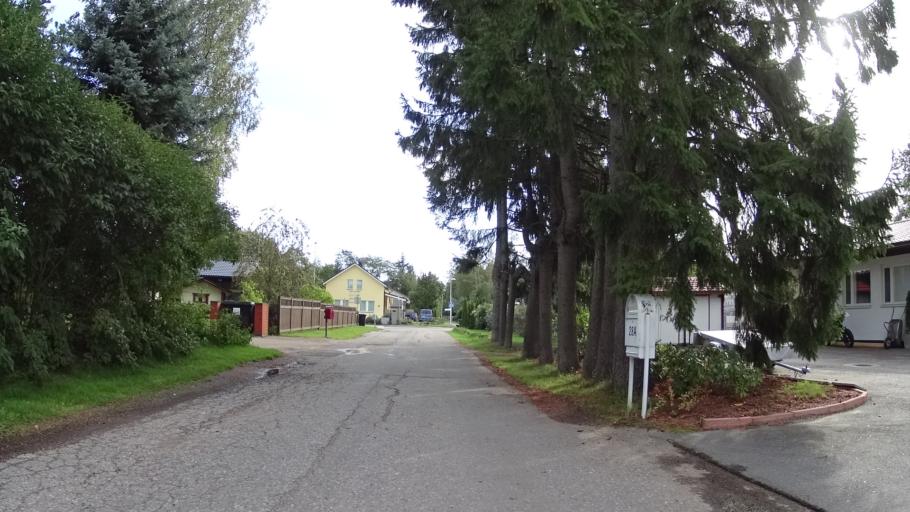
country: FI
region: Uusimaa
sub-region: Helsinki
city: Vantaa
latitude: 60.2961
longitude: 25.0034
